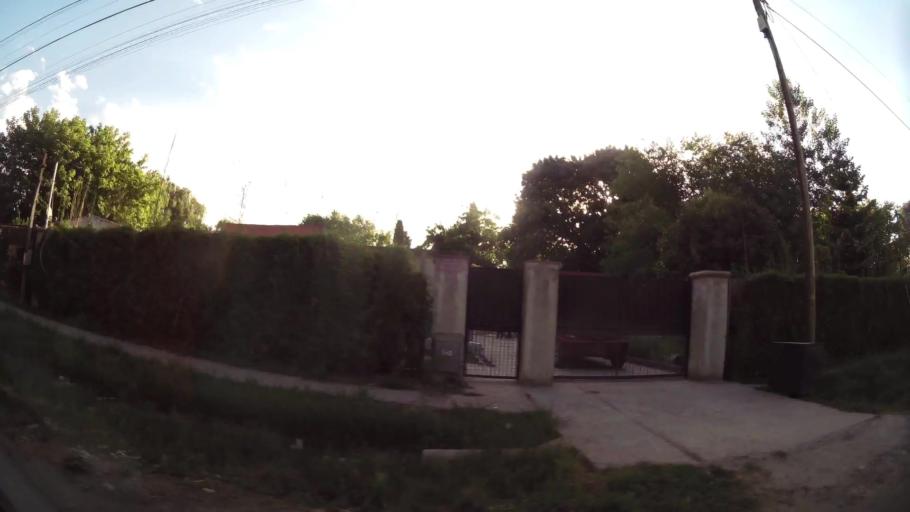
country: AR
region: Buenos Aires
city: Santa Catalina - Dique Lujan
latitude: -34.4682
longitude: -58.7468
